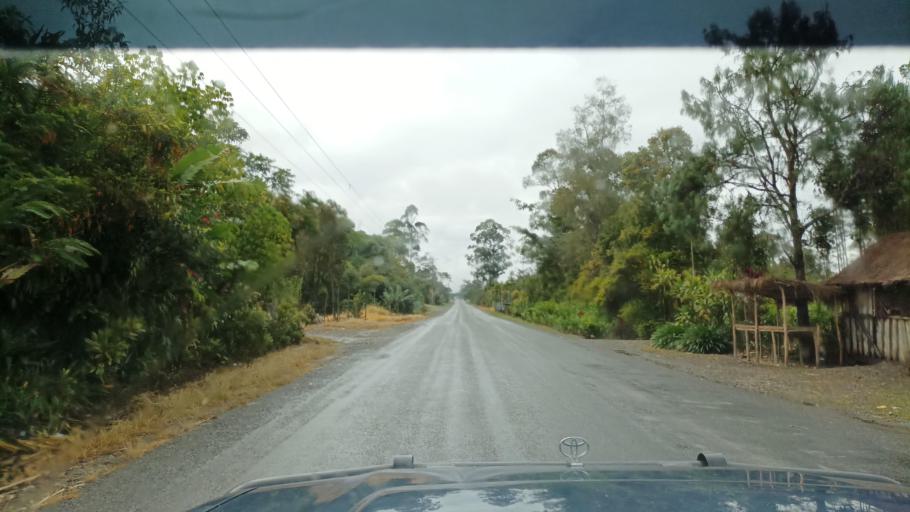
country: PG
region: Jiwaka
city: Minj
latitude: -5.8750
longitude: 144.6659
